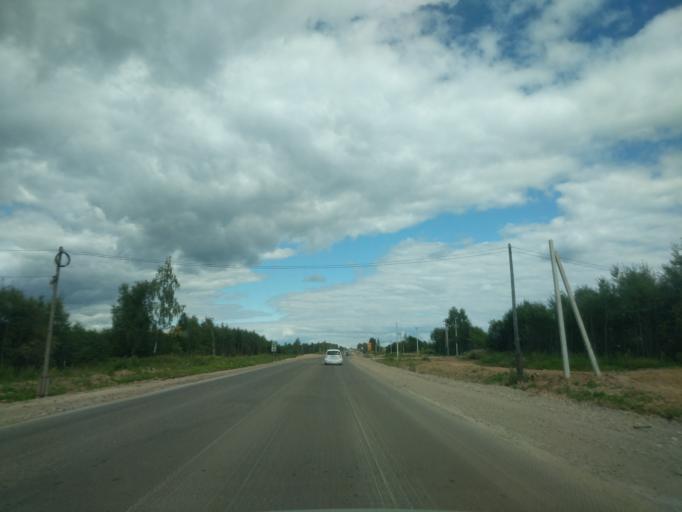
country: RU
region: Kostroma
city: Sudislavl'
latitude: 57.8638
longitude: 41.6242
